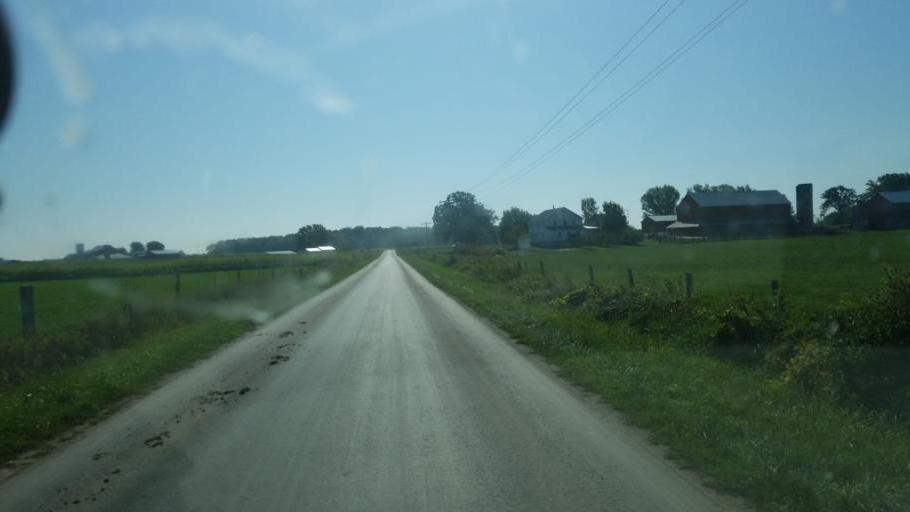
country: US
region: Ohio
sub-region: Hardin County
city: Kenton
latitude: 40.5646
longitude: -83.4462
